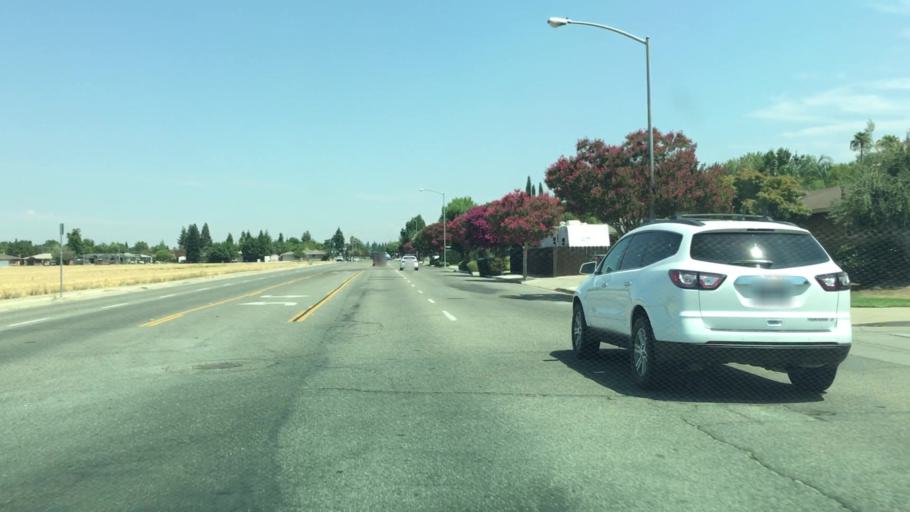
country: US
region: California
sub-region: Fresno County
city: Clovis
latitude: 36.8271
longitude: -119.7360
